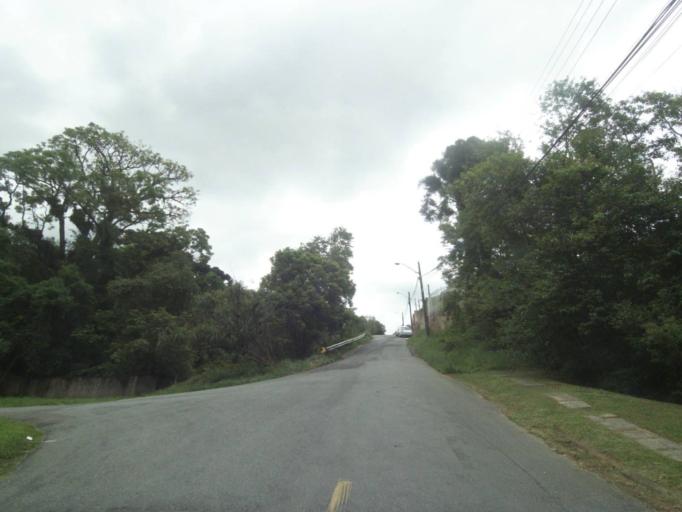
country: BR
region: Parana
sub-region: Curitiba
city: Curitiba
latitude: -25.3909
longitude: -49.2793
